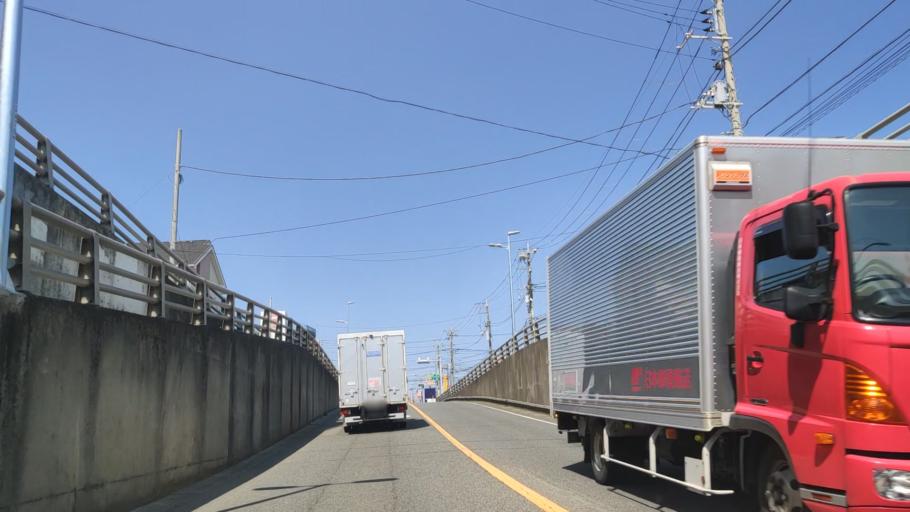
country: JP
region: Kanagawa
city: Chigasaki
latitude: 35.3314
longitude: 139.3771
